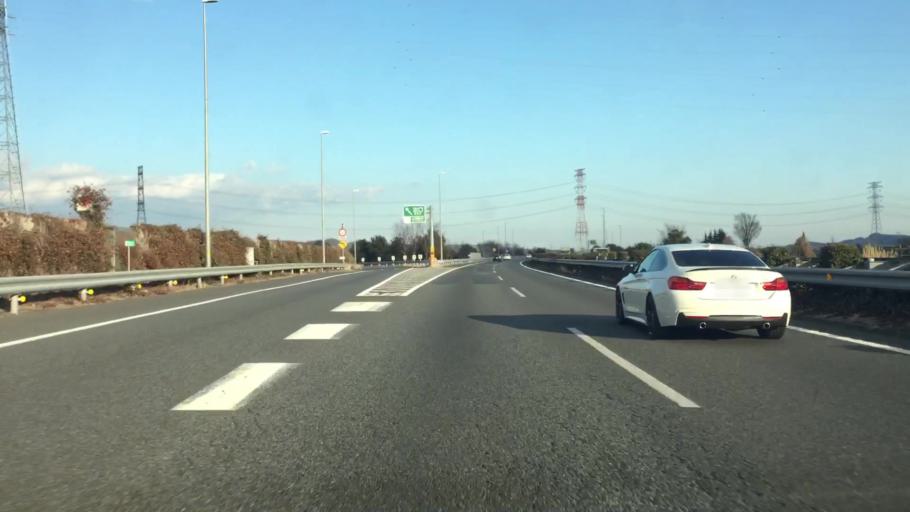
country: JP
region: Gunma
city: Kiryu
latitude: 36.3471
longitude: 139.2745
